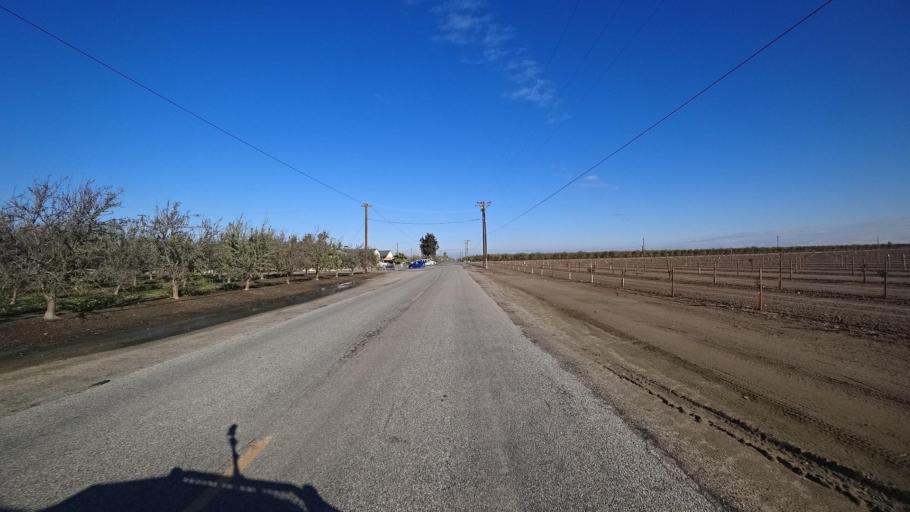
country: US
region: California
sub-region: Kern County
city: Delano
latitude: 35.7160
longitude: -119.3119
